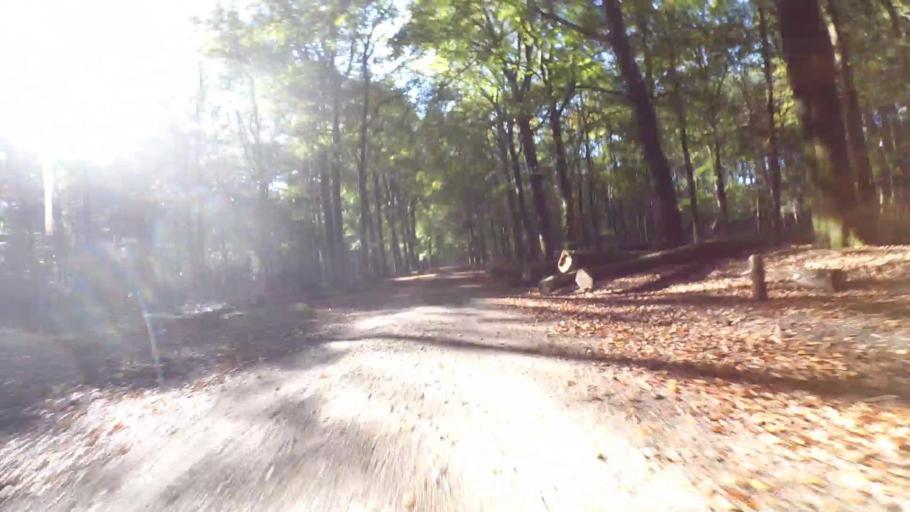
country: NL
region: Gelderland
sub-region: Gemeente Apeldoorn
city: Apeldoorn
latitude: 52.2283
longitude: 5.8774
